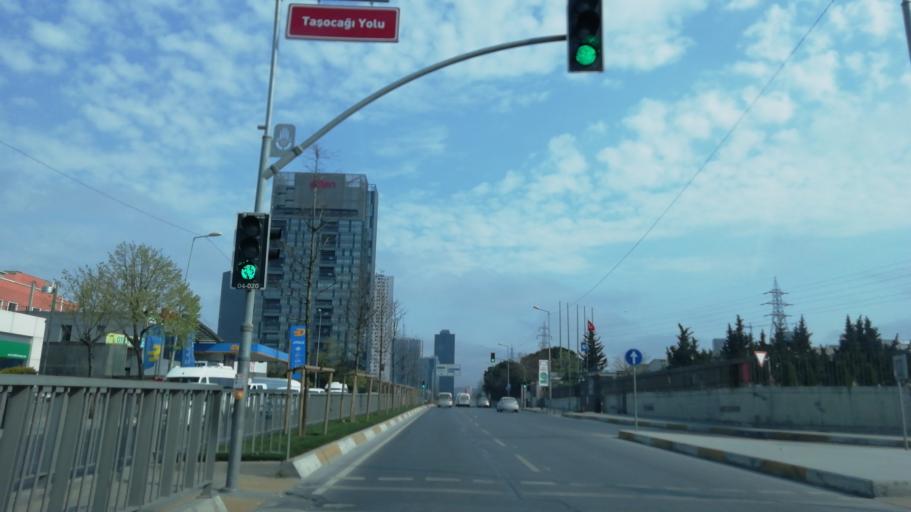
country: TR
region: Istanbul
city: Mahmutbey
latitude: 41.0494
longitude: 28.8123
